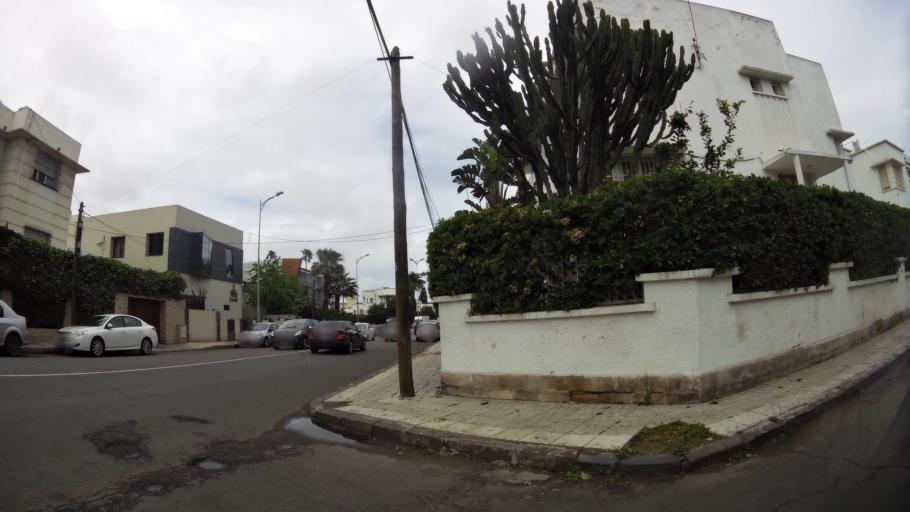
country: MA
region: Grand Casablanca
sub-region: Casablanca
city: Casablanca
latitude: 33.5799
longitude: -7.6097
